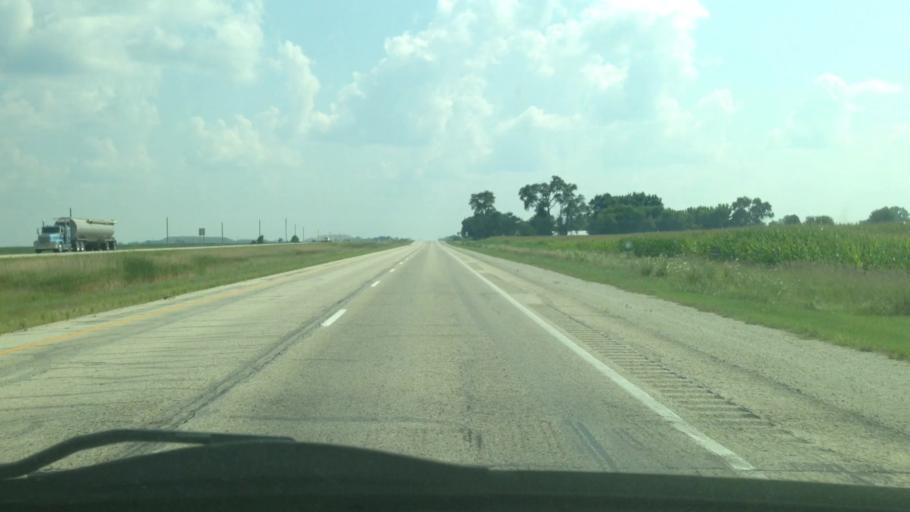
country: US
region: Iowa
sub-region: Bremer County
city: Tripoli
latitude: 42.8545
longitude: -92.3376
